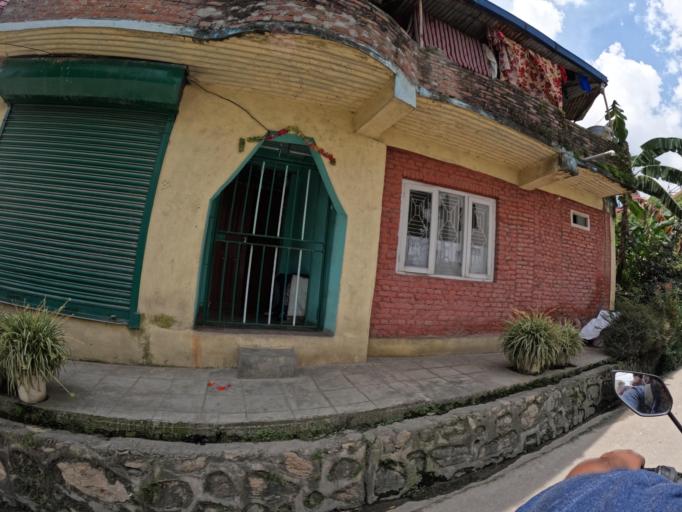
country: NP
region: Central Region
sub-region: Bagmati Zone
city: Kathmandu
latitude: 27.6786
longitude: 85.3660
